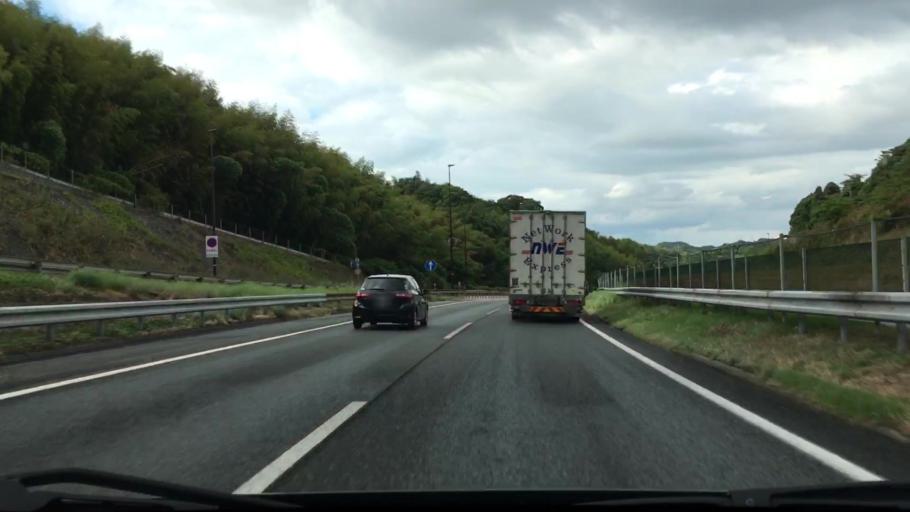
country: JP
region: Fukuoka
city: Nishifukuma
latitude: 33.7401
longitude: 130.5200
